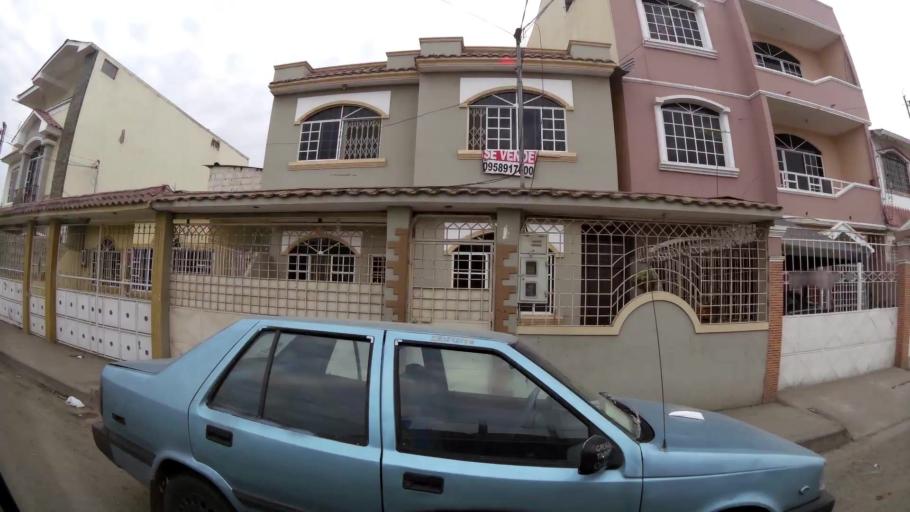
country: EC
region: El Oro
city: Machala
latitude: -3.2482
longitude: -79.9609
